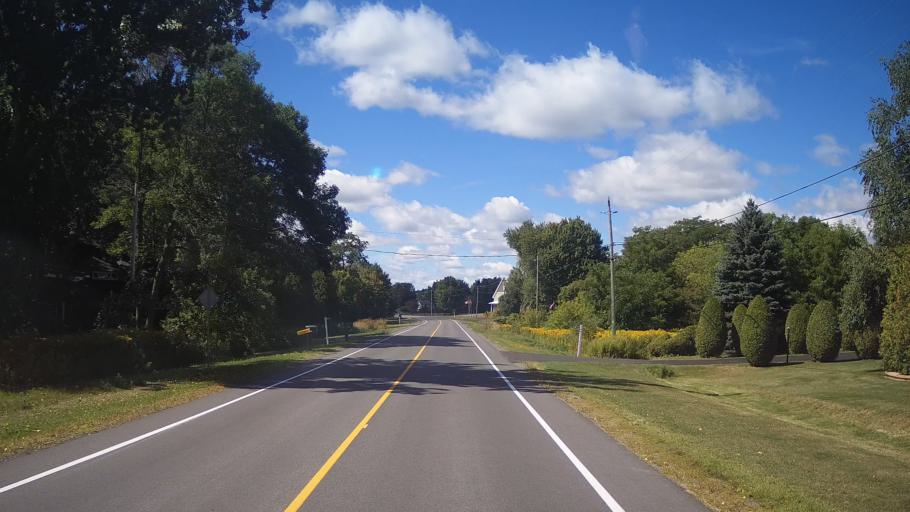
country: US
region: New York
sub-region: St. Lawrence County
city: Norfolk
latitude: 44.8616
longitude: -75.2614
